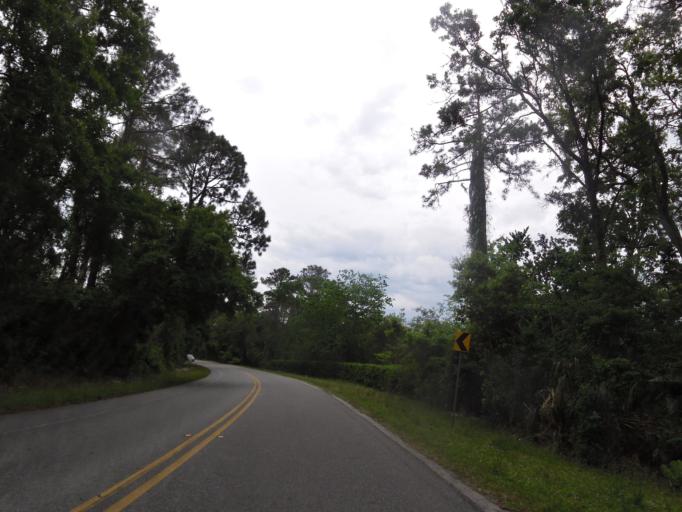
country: US
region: Florida
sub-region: Saint Johns County
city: Ponte Vedra Beach
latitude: 30.2262
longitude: -81.3967
